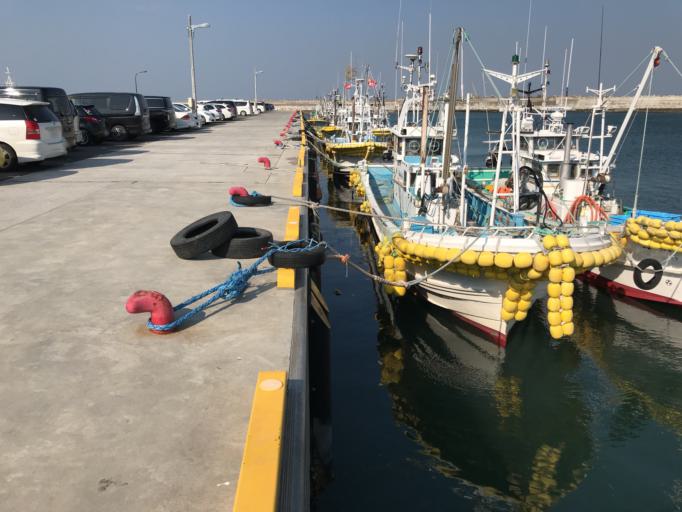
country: JP
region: Miyagi
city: Marumori
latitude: 37.8263
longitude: 140.9789
